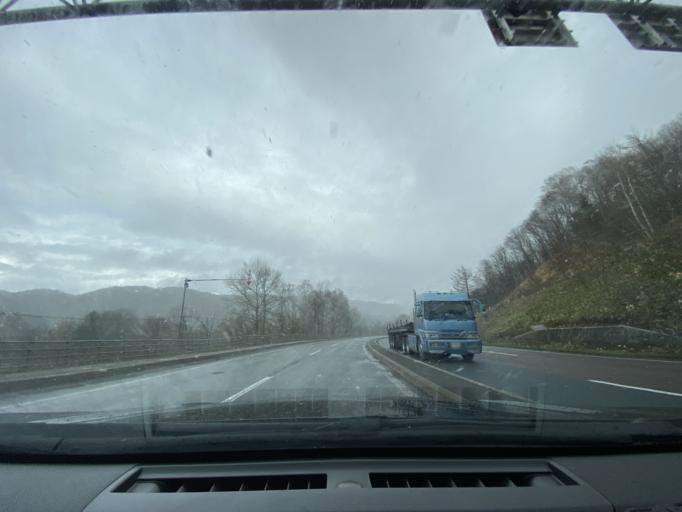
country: JP
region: Hokkaido
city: Fukagawa
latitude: 43.7281
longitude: 142.1879
